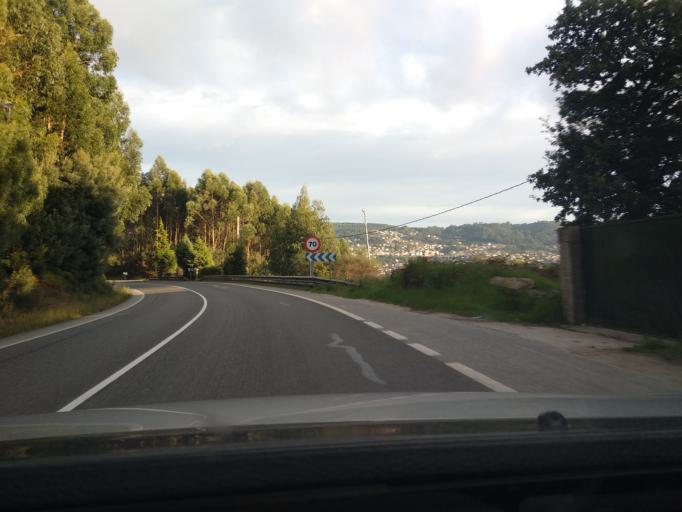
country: ES
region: Galicia
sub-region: Provincia de Pontevedra
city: Vigo
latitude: 42.2804
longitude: -8.6949
